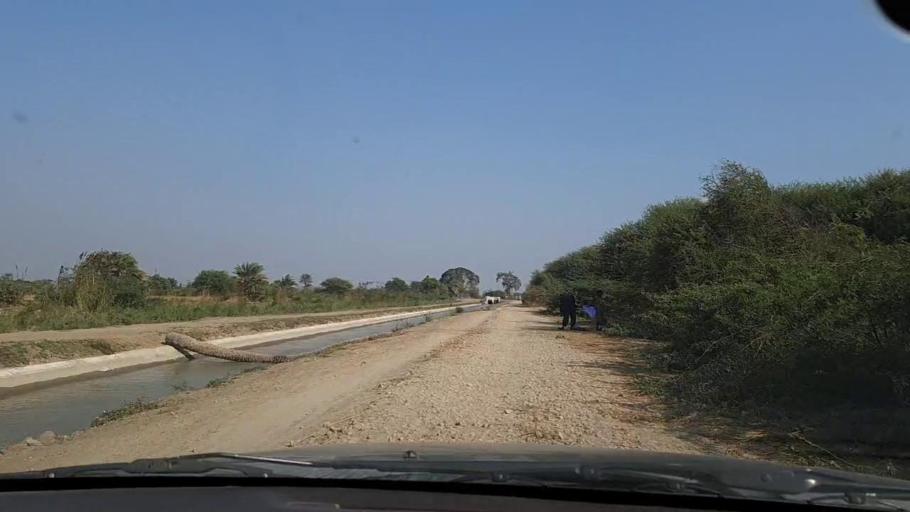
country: PK
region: Sindh
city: Mirpur Sakro
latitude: 24.3421
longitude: 67.7307
